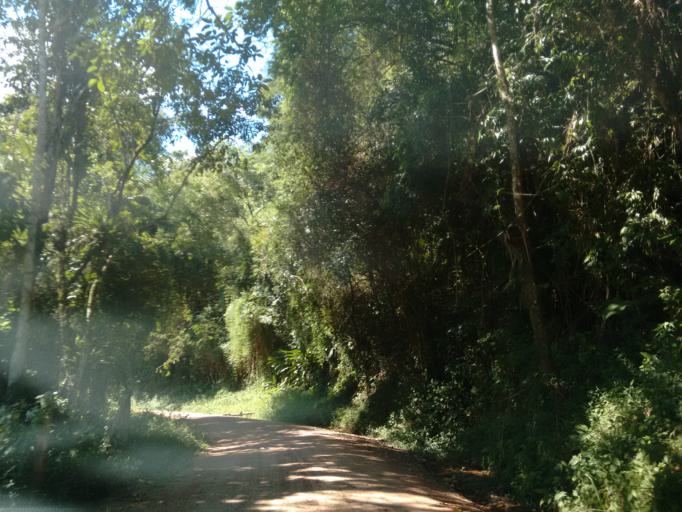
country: BR
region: Santa Catarina
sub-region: Indaial
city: Indaial
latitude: -26.9327
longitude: -49.1836
